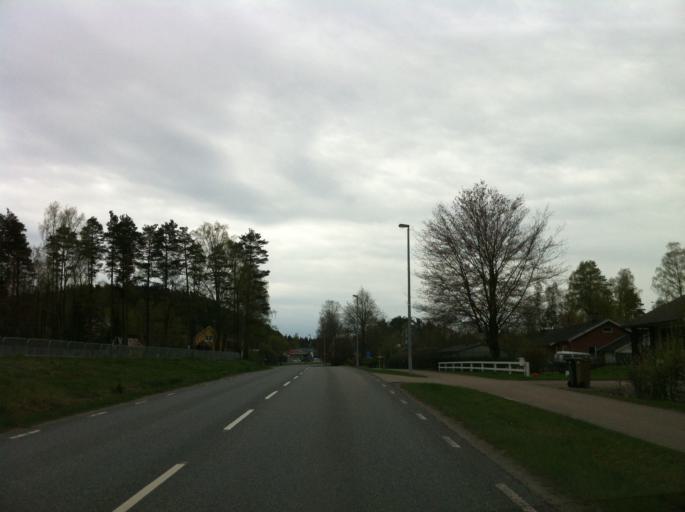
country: SE
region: Halland
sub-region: Halmstads Kommun
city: Getinge
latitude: 57.1299
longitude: 12.7162
